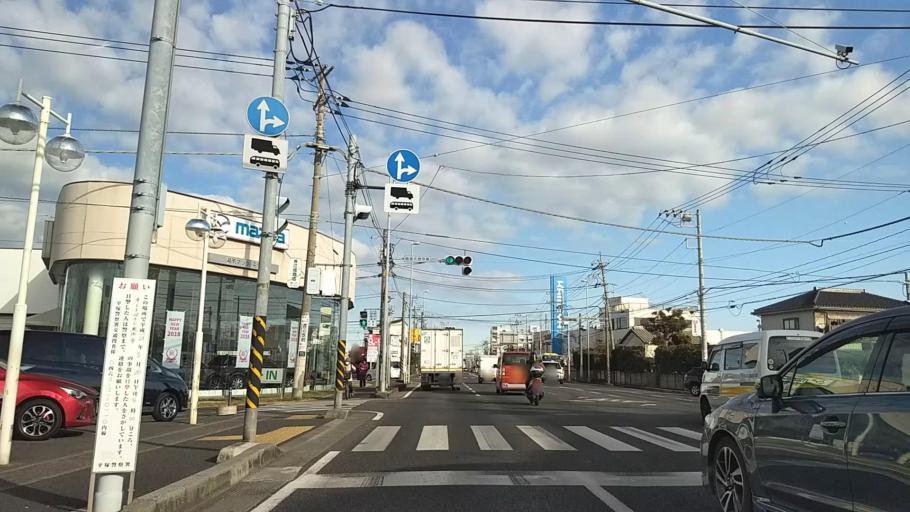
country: JP
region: Kanagawa
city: Hiratsuka
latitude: 35.3547
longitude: 139.3568
